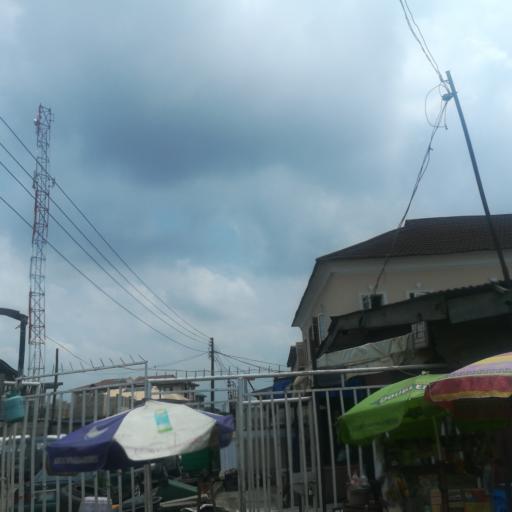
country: NG
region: Lagos
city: Ojota
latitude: 6.5851
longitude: 3.3802
